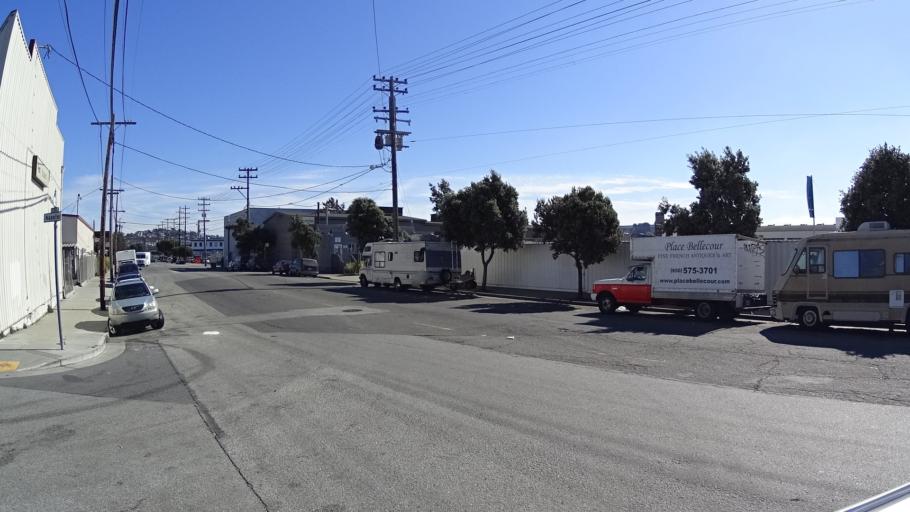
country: US
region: California
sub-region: San Francisco County
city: San Francisco
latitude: 37.7460
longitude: -122.4020
